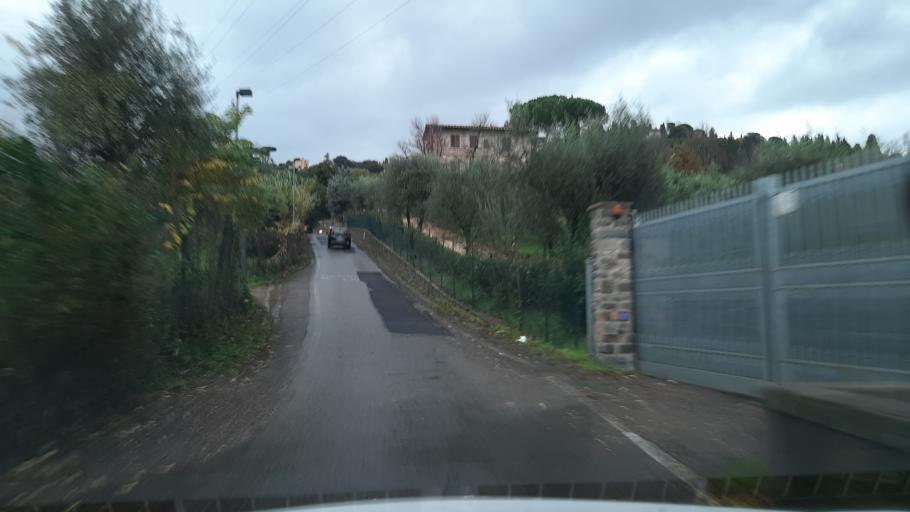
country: IT
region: Tuscany
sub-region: Province of Florence
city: Fiesole
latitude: 43.8063
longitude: 11.2685
